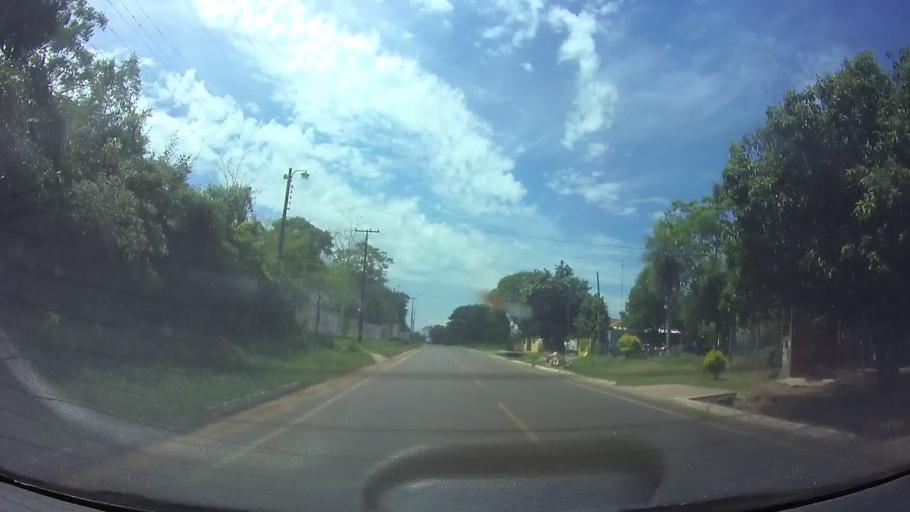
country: PY
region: Central
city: Limpio
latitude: -25.2225
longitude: -57.4484
